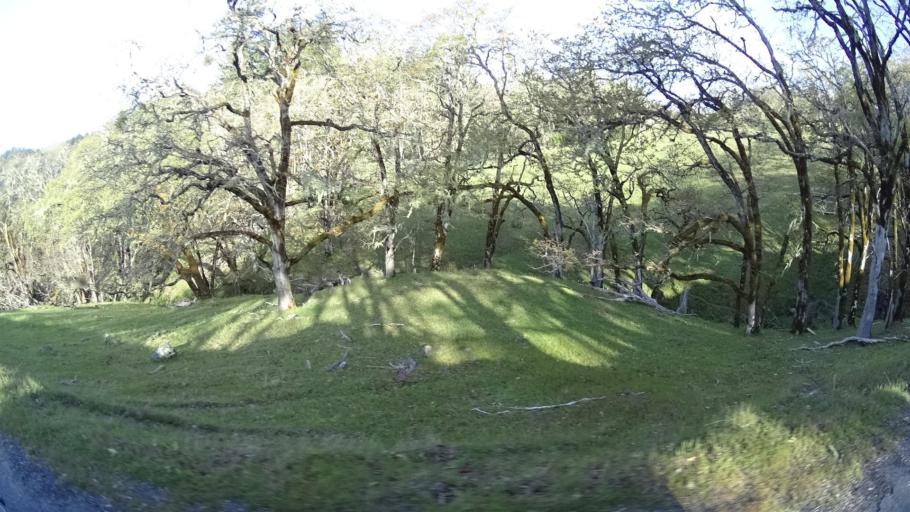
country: US
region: California
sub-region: Humboldt County
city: Blue Lake
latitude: 40.7156
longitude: -123.9375
